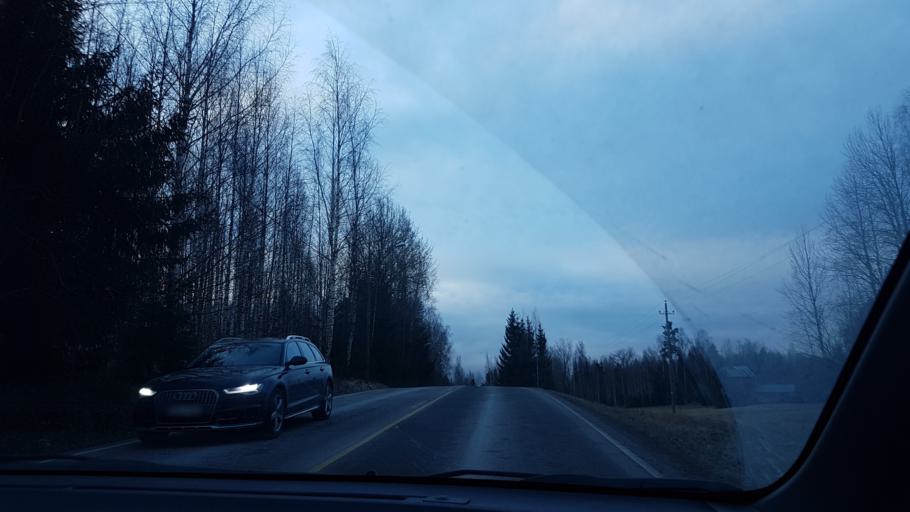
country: FI
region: Uusimaa
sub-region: Helsinki
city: Nurmijaervi
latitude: 60.3570
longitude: 24.7447
